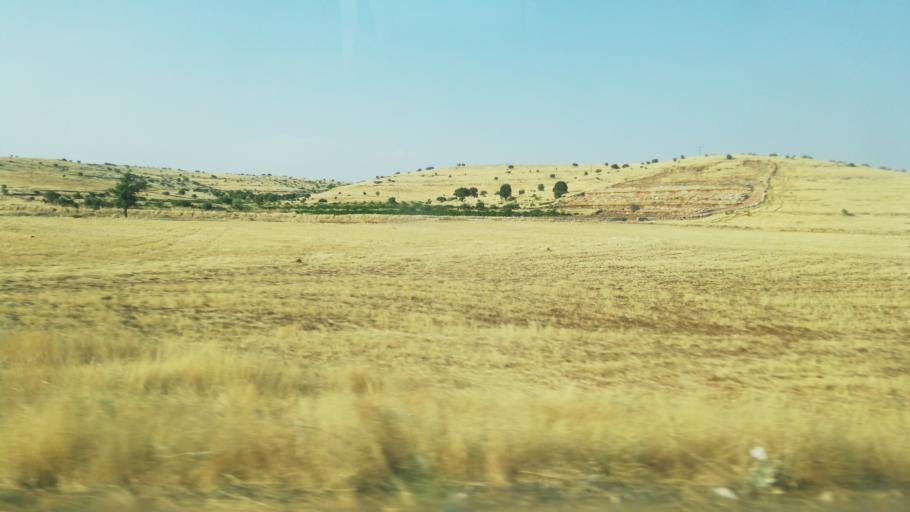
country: TR
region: Mardin
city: Acirli
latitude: 37.4520
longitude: 41.2595
